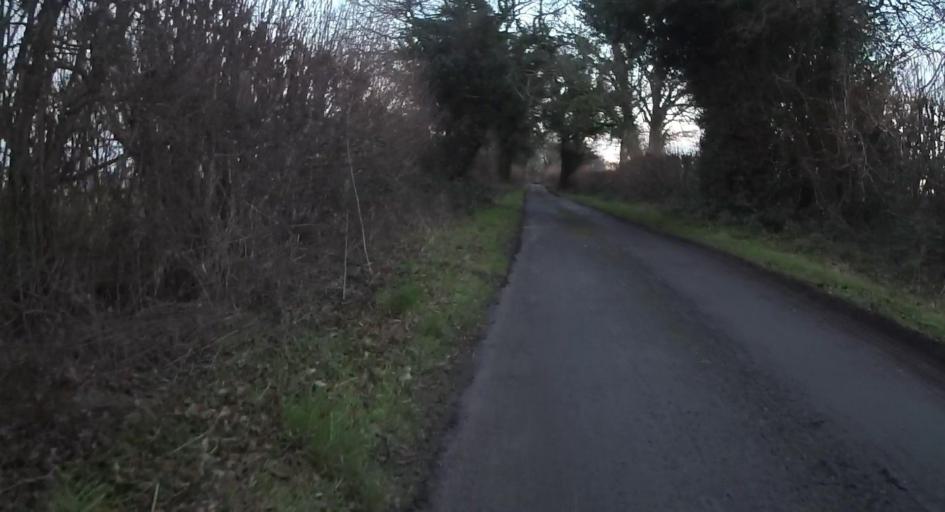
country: GB
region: England
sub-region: Hampshire
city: Swanmore
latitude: 51.0266
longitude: -1.1201
